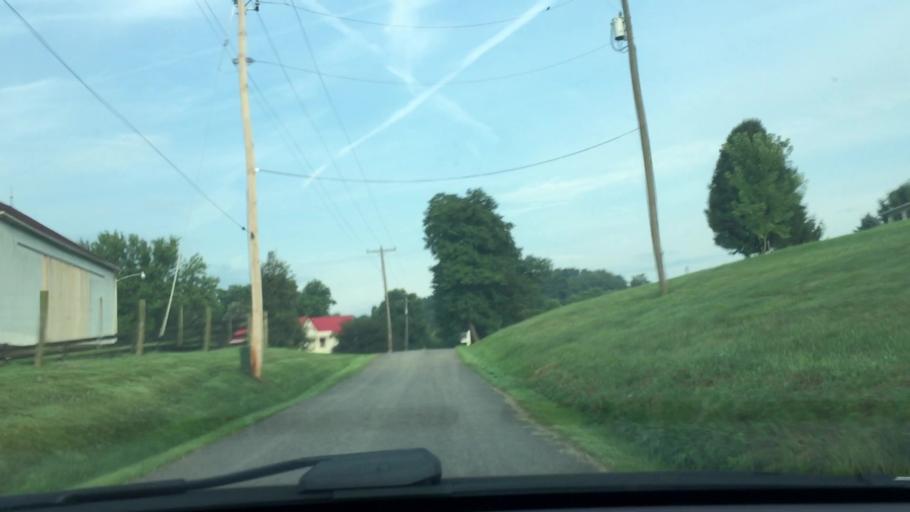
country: US
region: Pennsylvania
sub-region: Washington County
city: McMurray
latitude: 40.1764
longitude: -80.0987
